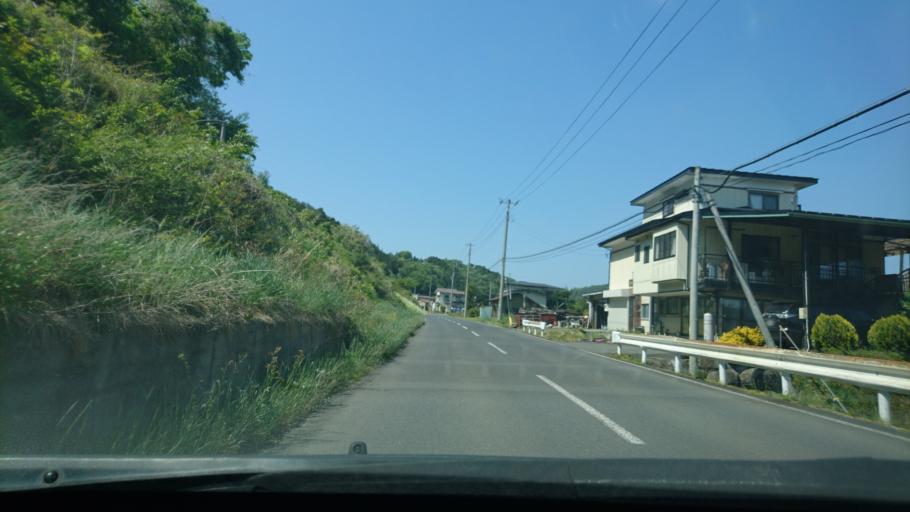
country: JP
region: Iwate
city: Ichinoseki
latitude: 38.9195
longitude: 141.2519
